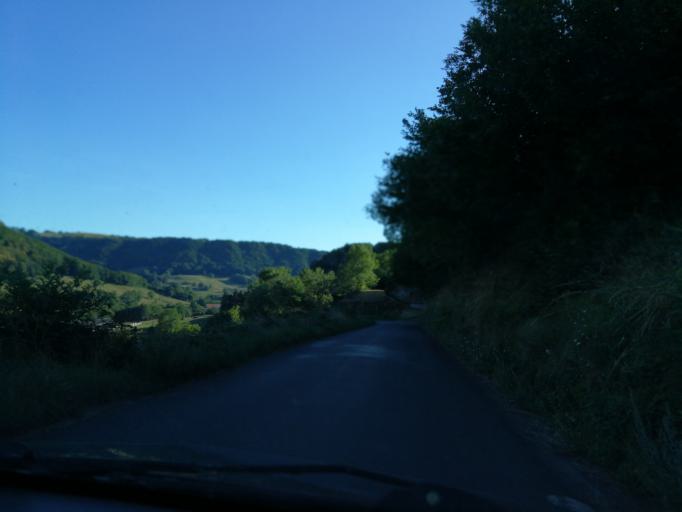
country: FR
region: Auvergne
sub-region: Departement du Cantal
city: Saint-Cernin
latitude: 45.1352
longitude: 2.5002
